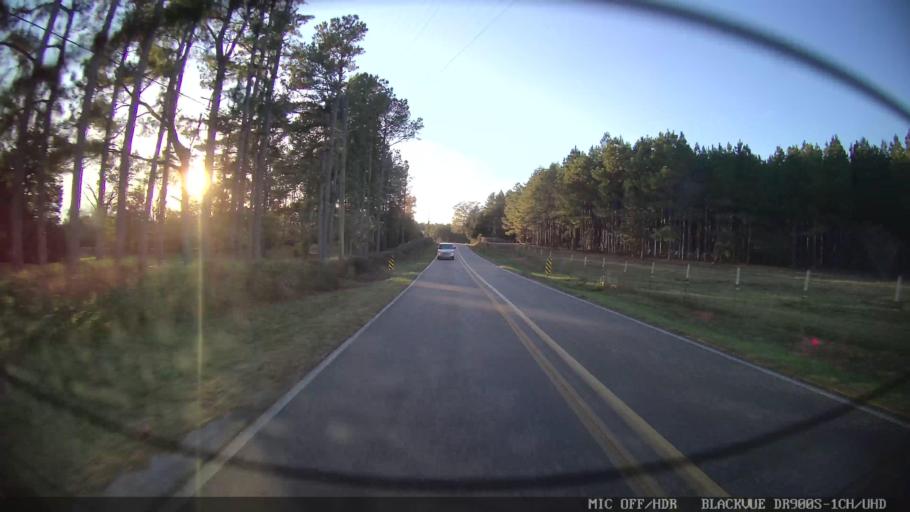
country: US
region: Mississippi
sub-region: Lamar County
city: Lumberton
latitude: 30.9980
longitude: -89.4025
